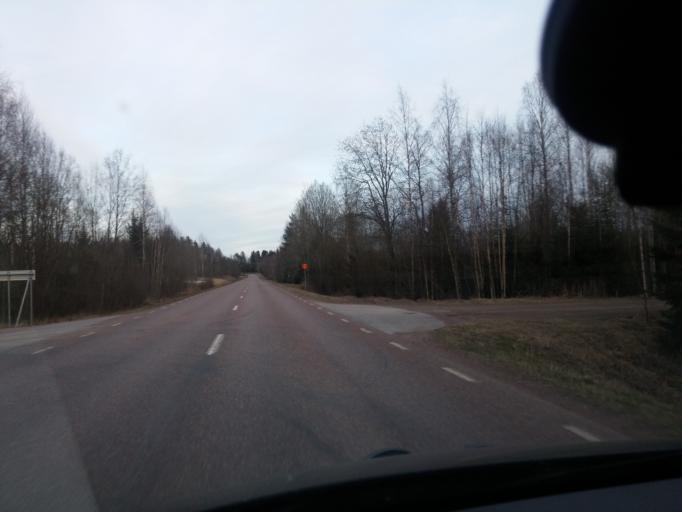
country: SE
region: Dalarna
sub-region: Faluns Kommun
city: Bjursas
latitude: 60.7270
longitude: 15.4324
